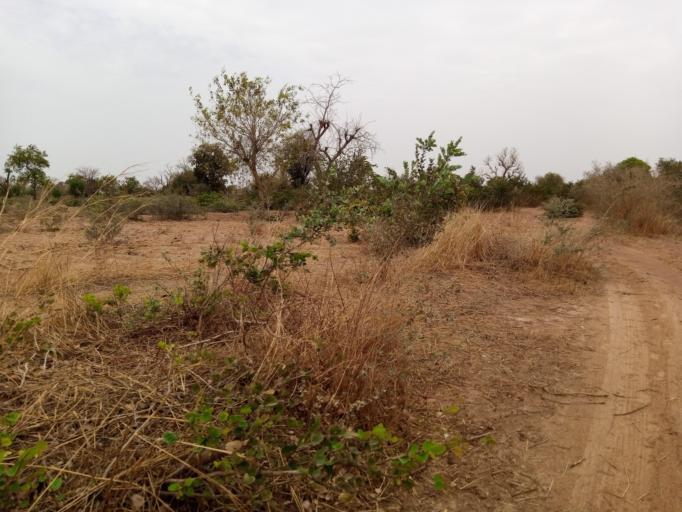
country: BF
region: Boucle du Mouhoun
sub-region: Province de la Kossi
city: Nouna
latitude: 12.8467
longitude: -4.0779
